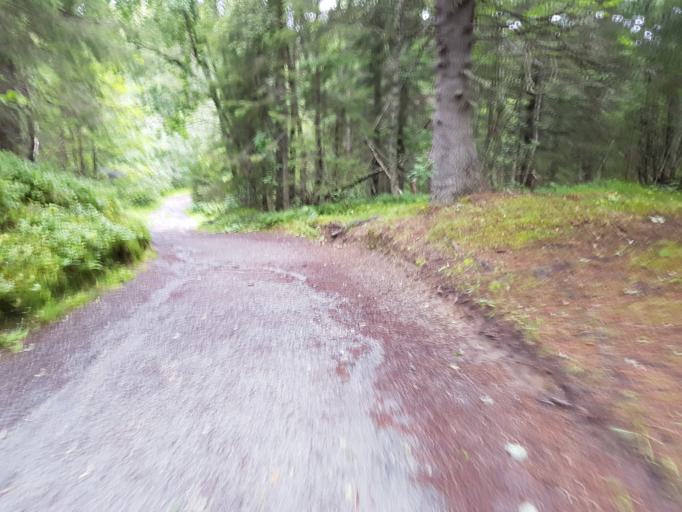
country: NO
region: Sor-Trondelag
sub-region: Trondheim
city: Trondheim
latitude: 63.3980
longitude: 10.4677
